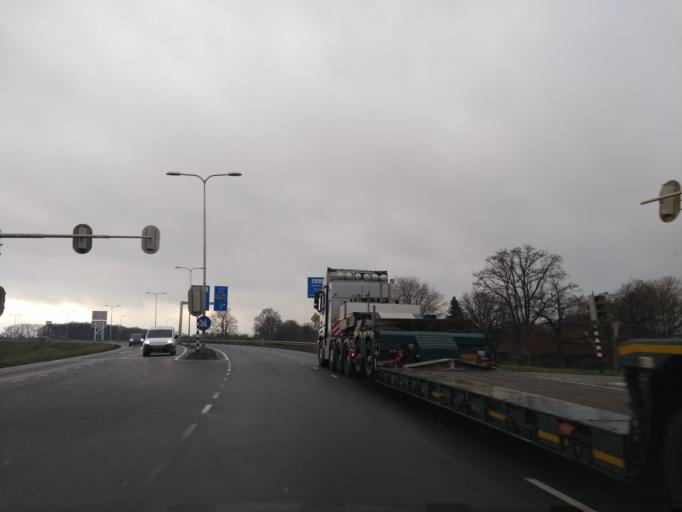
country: NL
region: Overijssel
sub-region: Gemeente Wierden
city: Wierden
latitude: 52.3477
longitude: 6.6079
